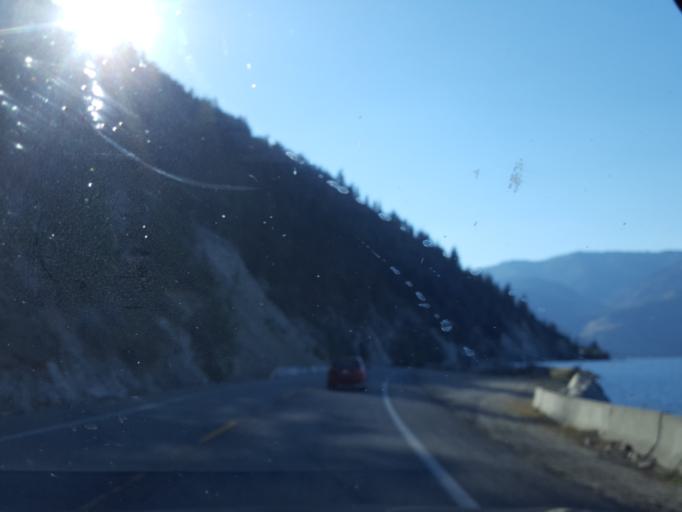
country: US
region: Washington
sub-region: Chelan County
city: Manson
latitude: 47.8602
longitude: -120.1658
